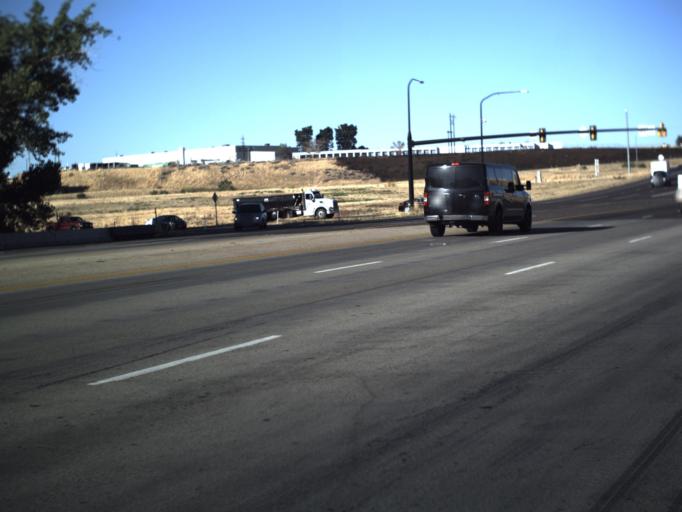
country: US
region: Utah
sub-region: Weber County
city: South Ogden
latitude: 41.2059
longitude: -111.9906
